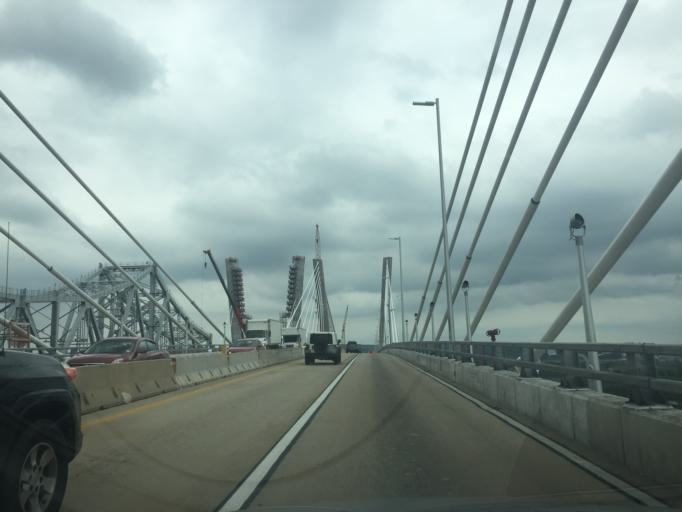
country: US
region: New Jersey
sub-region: Union County
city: Elizabeth
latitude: 40.6358
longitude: -74.1985
